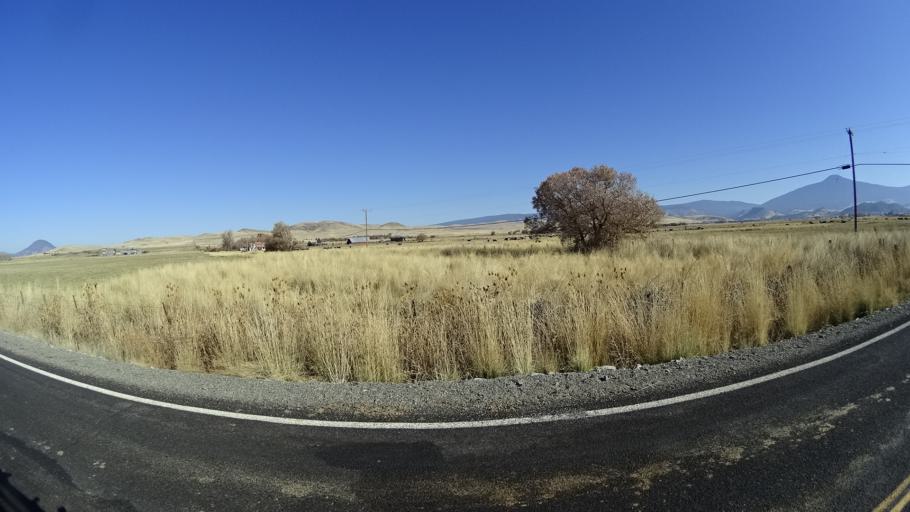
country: US
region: California
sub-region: Siskiyou County
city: Montague
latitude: 41.7123
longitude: -122.4383
